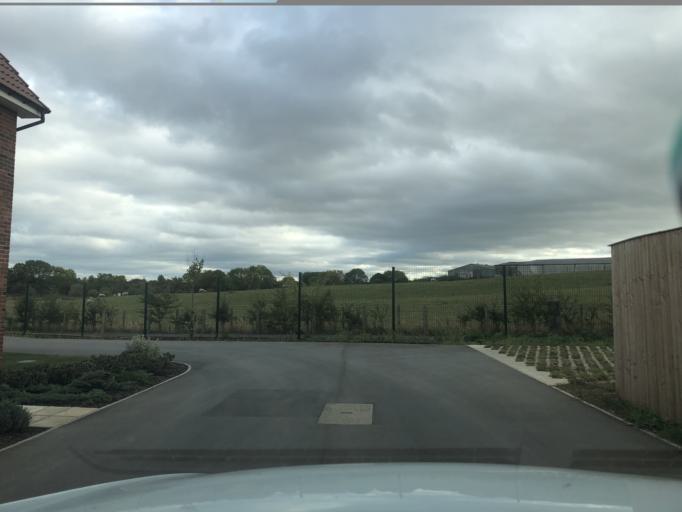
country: GB
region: England
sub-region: North Yorkshire
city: Northallerton
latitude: 54.3429
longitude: -1.4447
